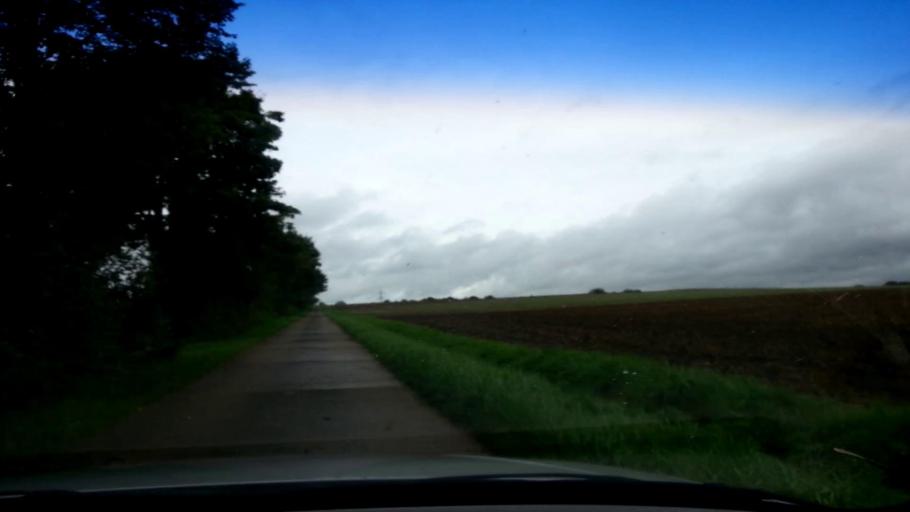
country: DE
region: Bavaria
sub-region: Upper Franconia
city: Memmelsdorf
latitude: 49.9501
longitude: 10.9804
